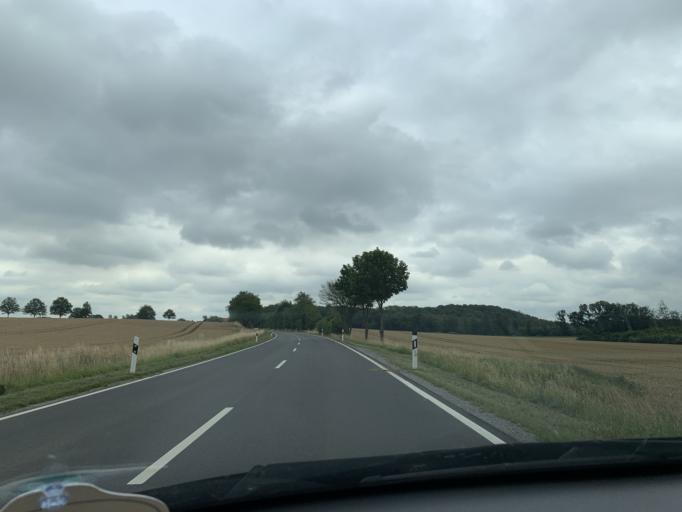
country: DE
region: North Rhine-Westphalia
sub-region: Regierungsbezirk Munster
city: Wadersloh
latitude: 51.7583
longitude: 8.1873
